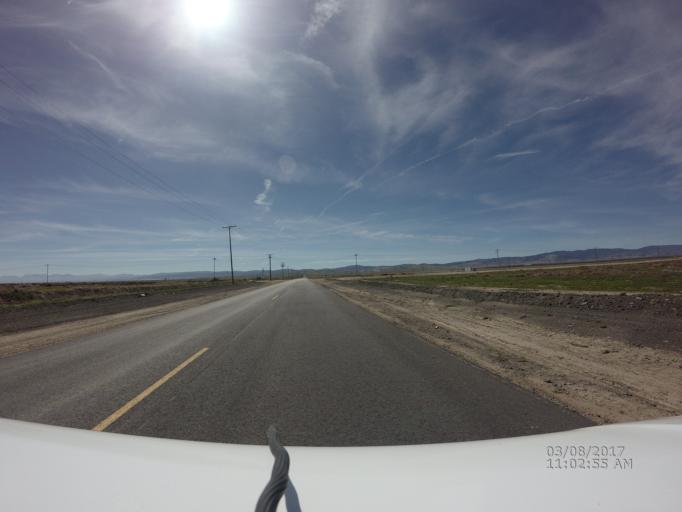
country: US
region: California
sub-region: Los Angeles County
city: Green Valley
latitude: 34.8057
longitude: -118.3790
